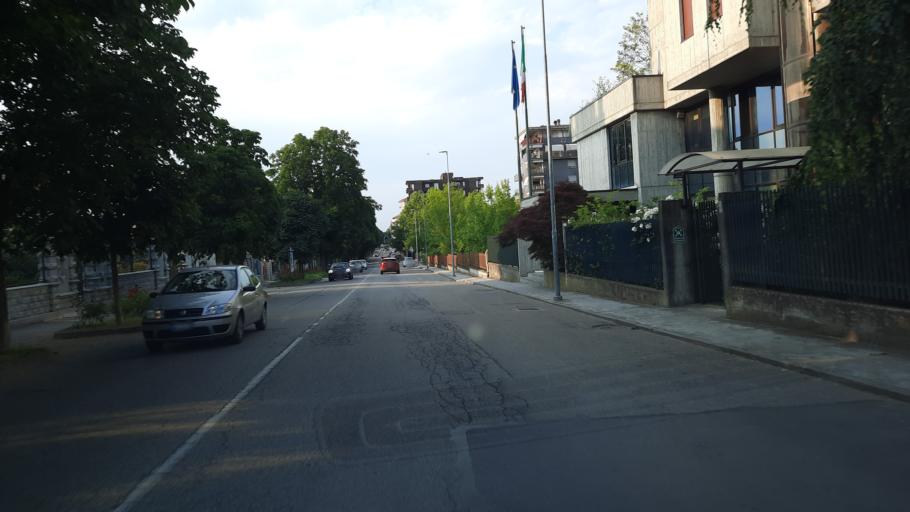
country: IT
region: Piedmont
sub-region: Provincia di Alessandria
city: Casale Monferrato
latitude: 45.1263
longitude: 8.4468
